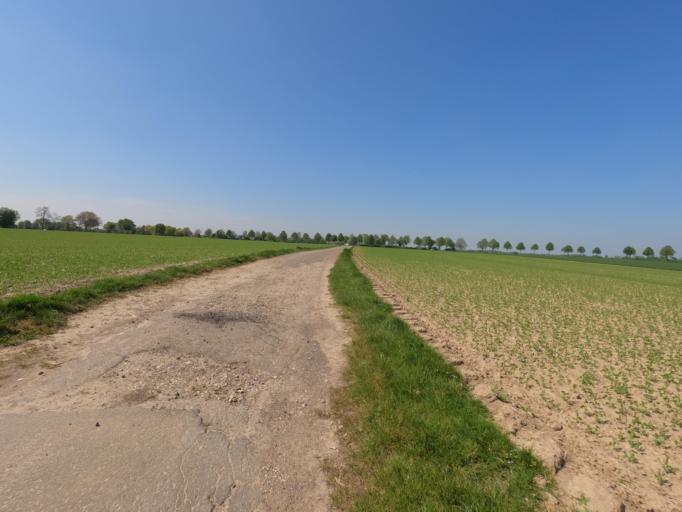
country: DE
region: North Rhine-Westphalia
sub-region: Regierungsbezirk Koln
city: Ubach-Palenberg
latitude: 50.9504
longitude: 6.0938
